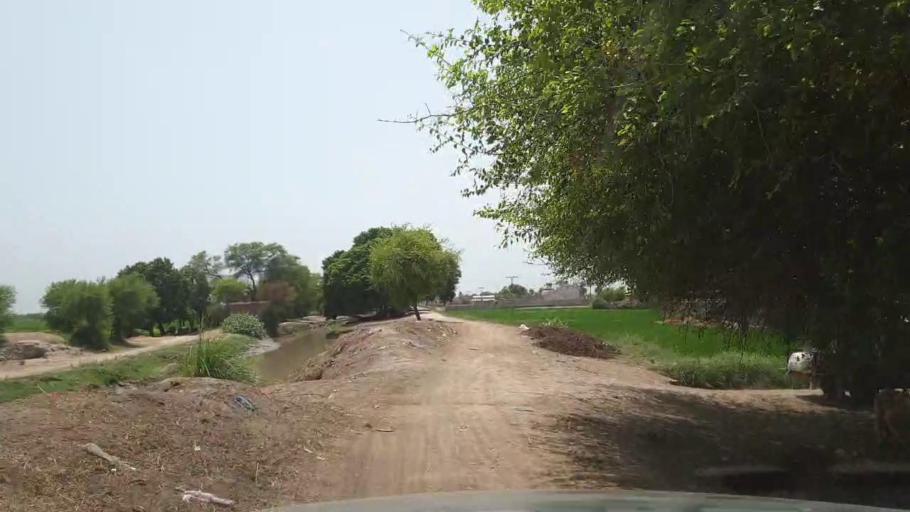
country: PK
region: Sindh
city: Ratodero
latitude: 27.7907
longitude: 68.3386
